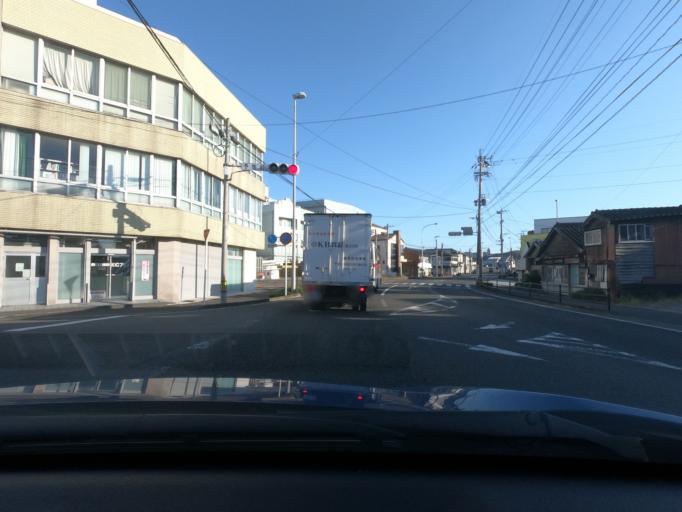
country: JP
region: Kagoshima
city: Akune
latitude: 32.0183
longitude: 130.1969
